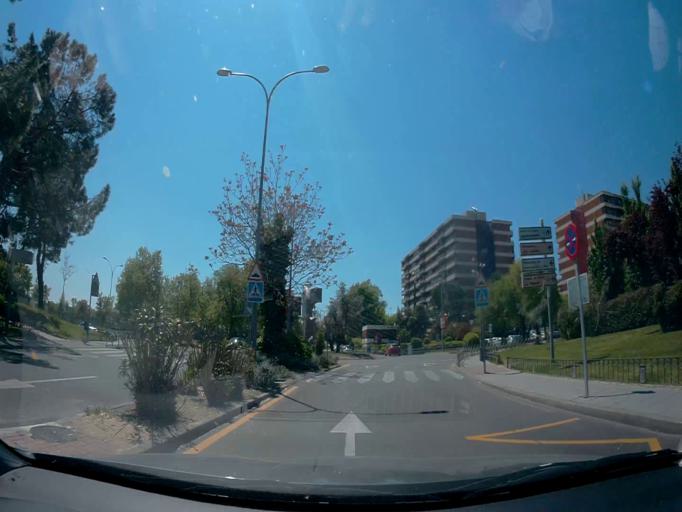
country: ES
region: Madrid
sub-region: Provincia de Madrid
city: Alcorcon
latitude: 40.3412
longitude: -3.8163
